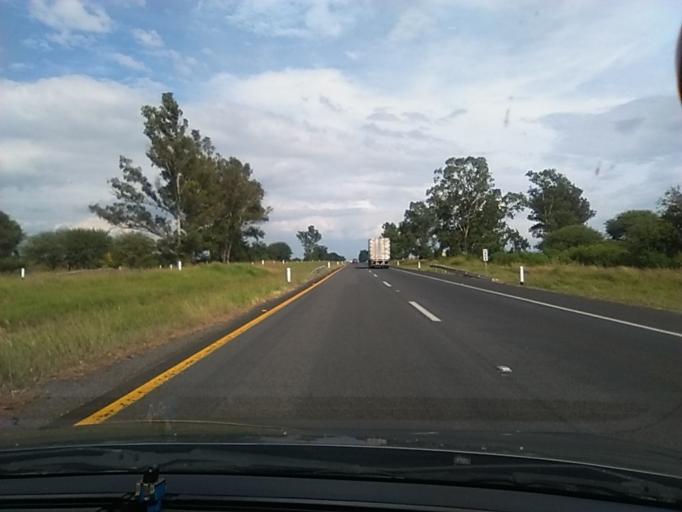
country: MX
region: Jalisco
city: La Barca
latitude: 20.3222
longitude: -102.5549
